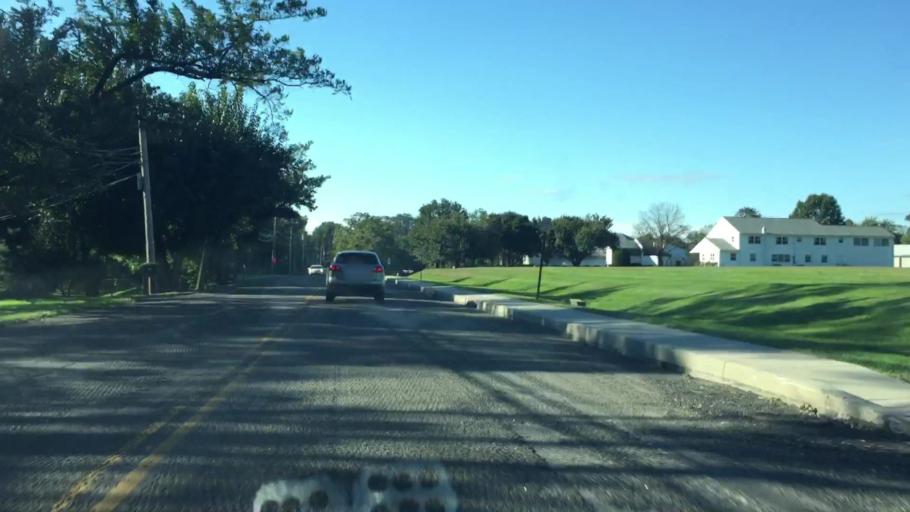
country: US
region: Pennsylvania
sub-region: Delaware County
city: Boothwyn
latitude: 39.8451
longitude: -75.4453
